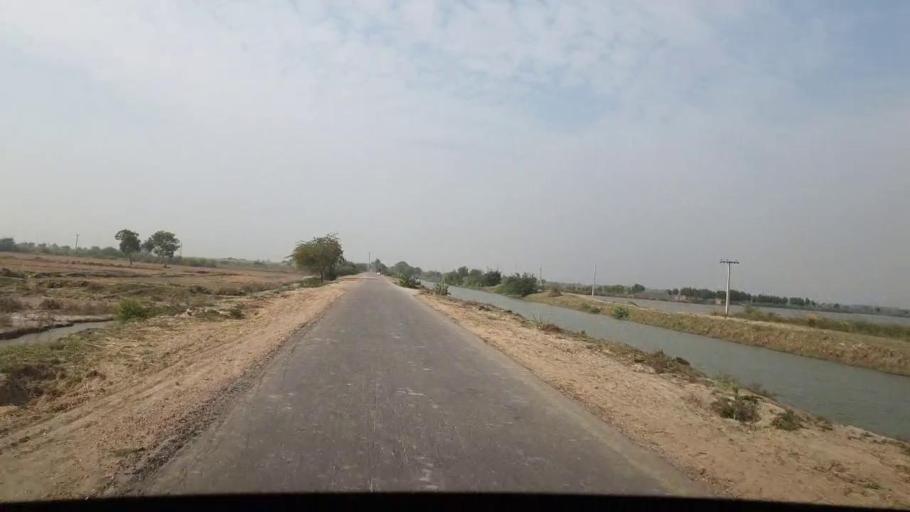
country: PK
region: Sindh
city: Chuhar Jamali
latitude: 24.3927
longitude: 67.9591
